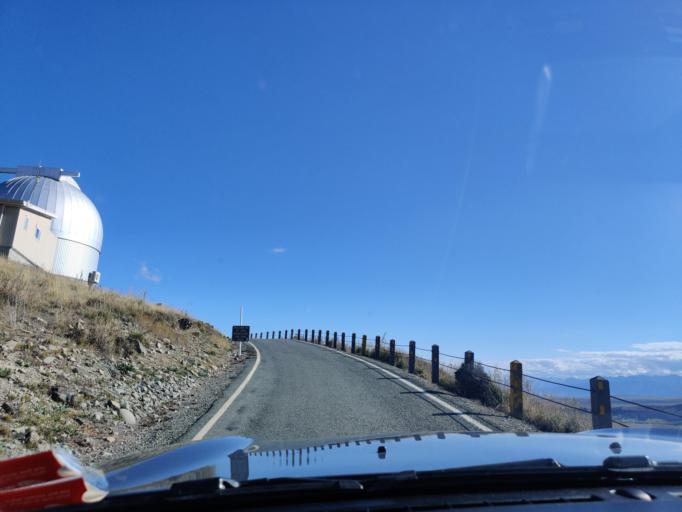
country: NZ
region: Canterbury
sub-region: Timaru District
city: Pleasant Point
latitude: -43.9847
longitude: 170.4642
